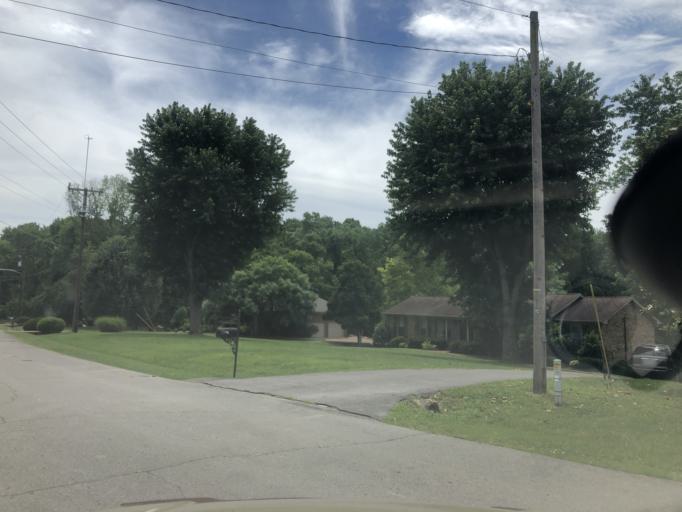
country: US
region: Tennessee
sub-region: Davidson County
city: Lakewood
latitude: 36.2587
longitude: -86.5933
